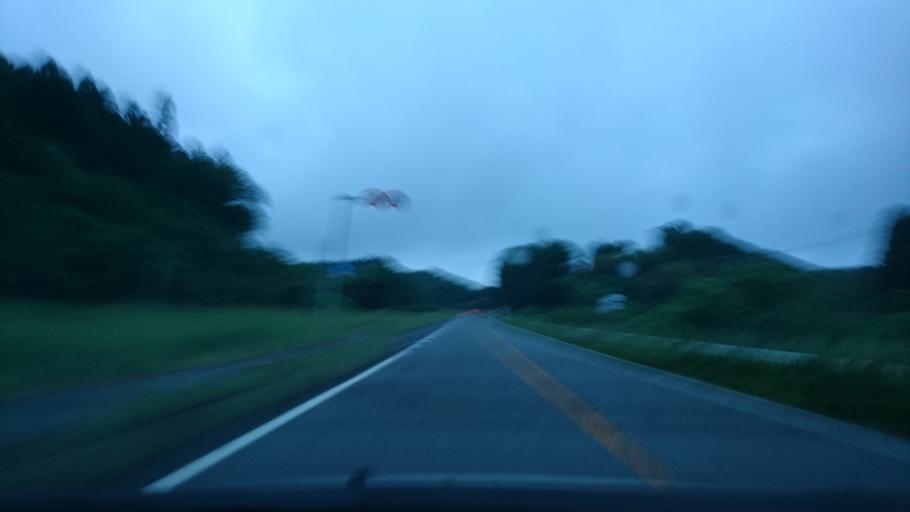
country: JP
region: Iwate
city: Ichinoseki
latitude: 38.8654
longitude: 141.1076
